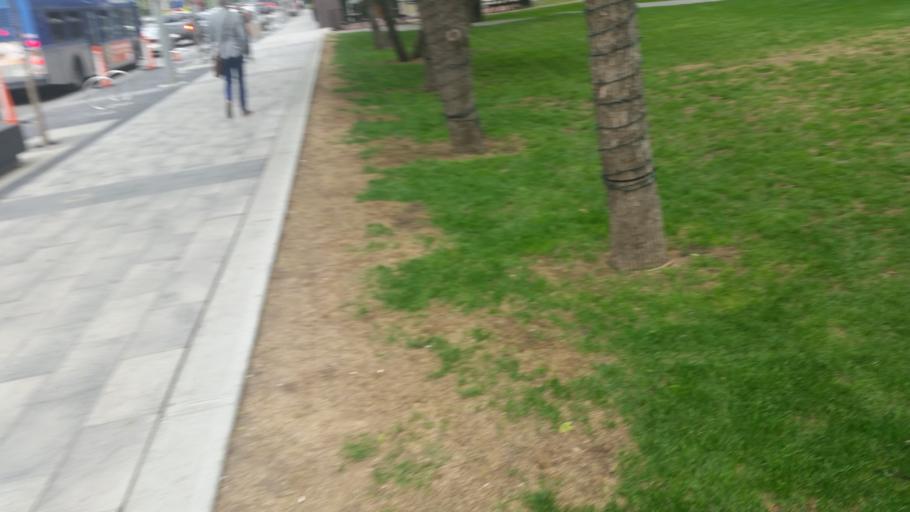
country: CA
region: Alberta
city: Edmonton
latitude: 53.5410
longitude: -113.4954
